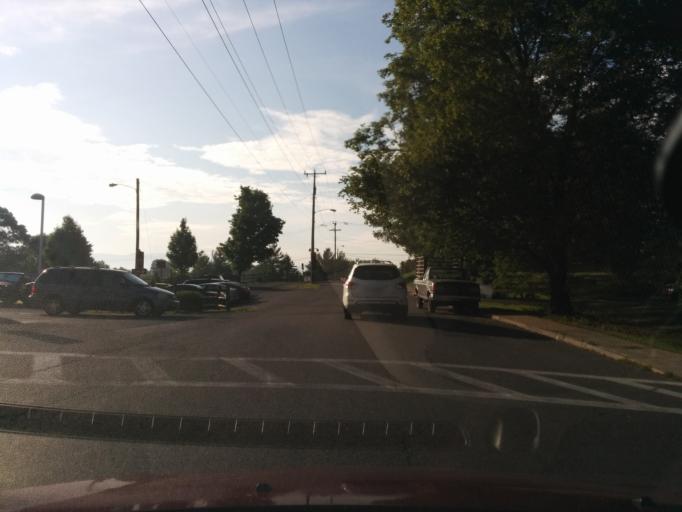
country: US
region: Virginia
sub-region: City of Lexington
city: Lexington
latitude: 37.7856
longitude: -79.4342
